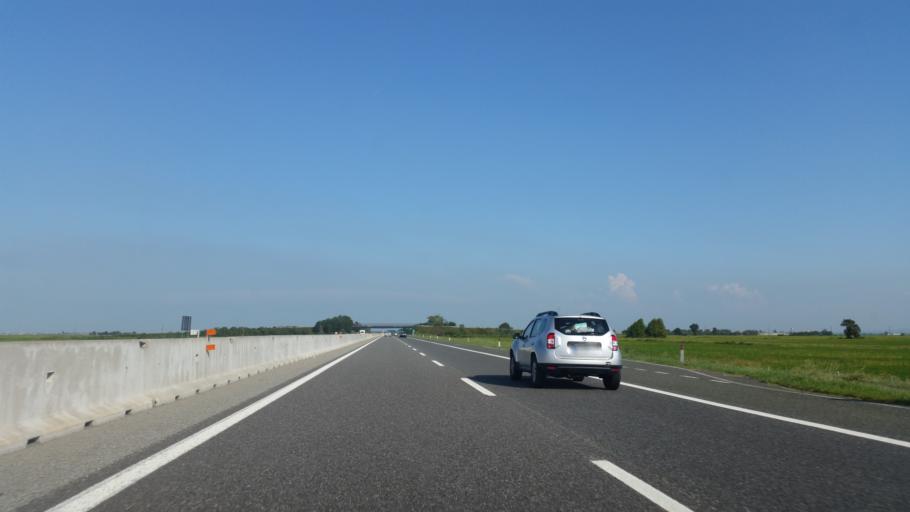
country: IT
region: Piedmont
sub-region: Provincia di Vercelli
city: Salasco
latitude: 45.3186
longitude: 8.2617
